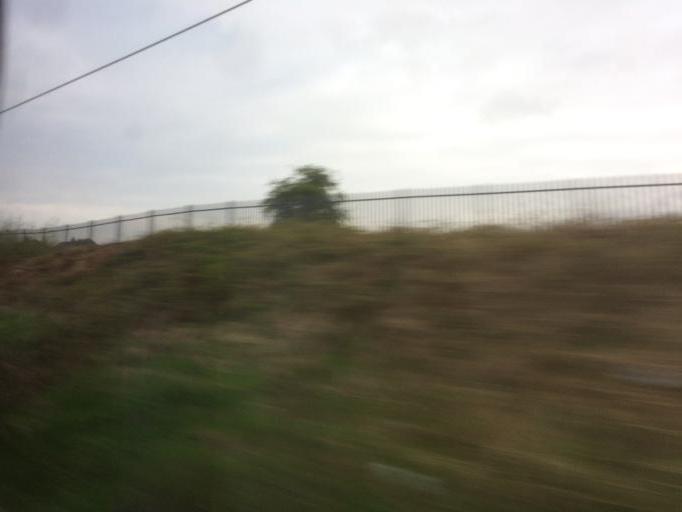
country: GB
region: Scotland
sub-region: East Dunbartonshire
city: Bishopbriggs
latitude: 55.9106
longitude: -4.2069
